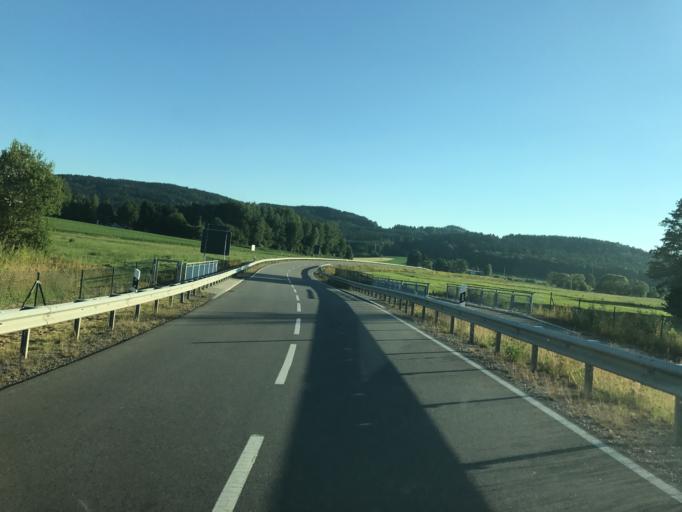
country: DE
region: Bavaria
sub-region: Upper Palatinate
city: Waldmunchen
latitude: 49.3815
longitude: 12.6902
